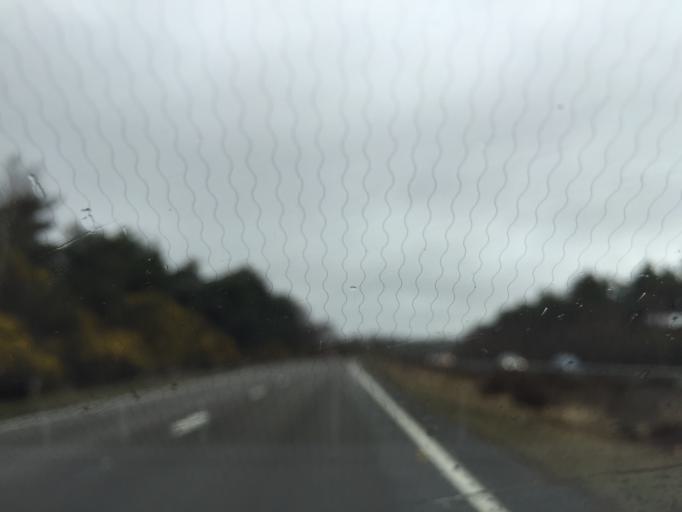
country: GB
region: England
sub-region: Hampshire
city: Cadnam
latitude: 50.8918
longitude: -1.6638
